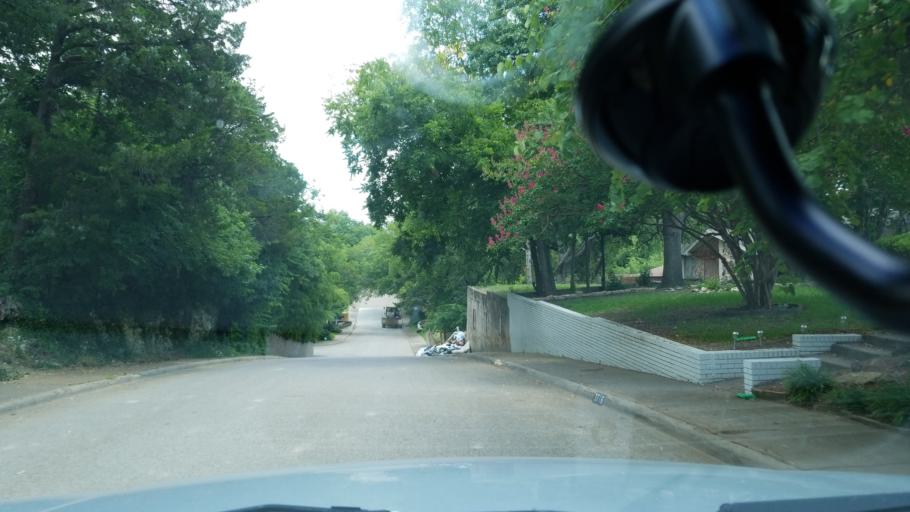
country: US
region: Texas
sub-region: Dallas County
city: Cockrell Hill
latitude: 32.7024
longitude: -96.8813
